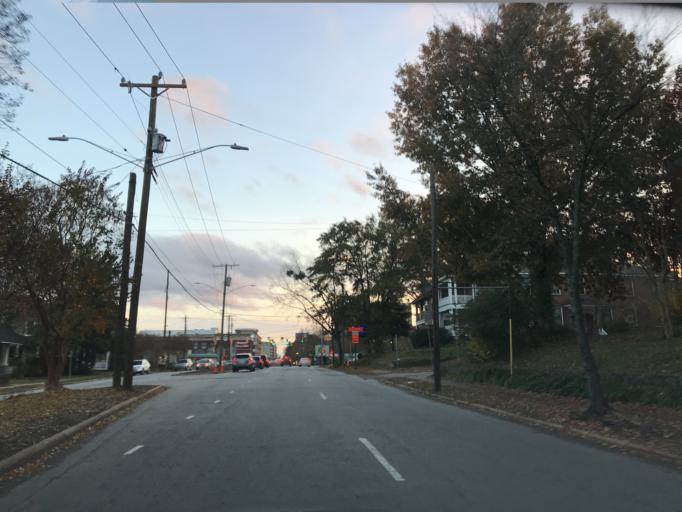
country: US
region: North Carolina
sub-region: Wake County
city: West Raleigh
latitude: 35.7898
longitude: -78.6472
